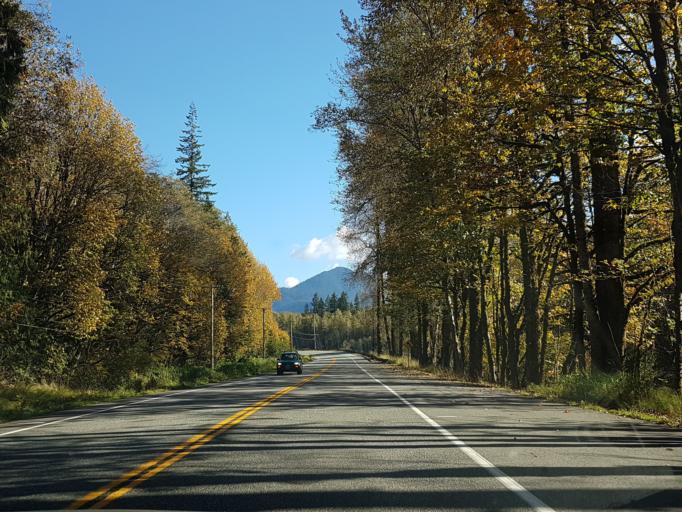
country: US
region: Washington
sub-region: Snohomish County
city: Gold Bar
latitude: 47.7478
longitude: -121.4500
